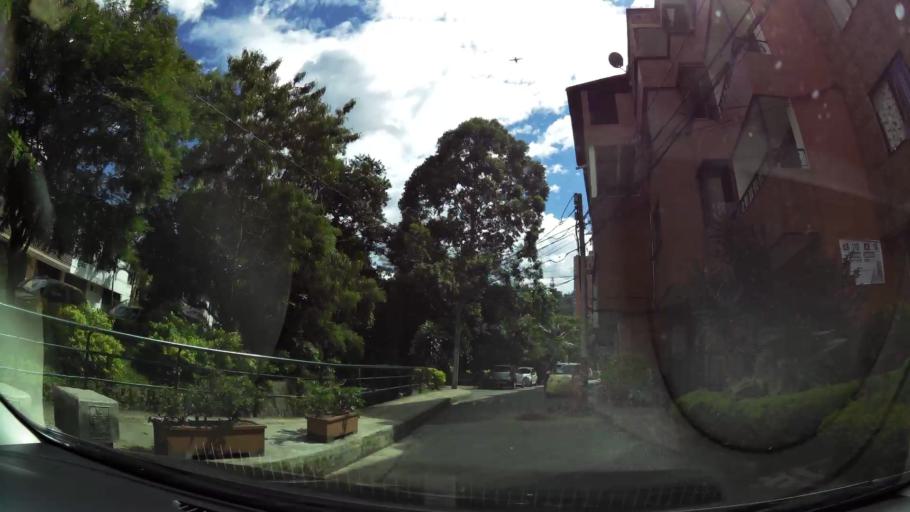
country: CO
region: Antioquia
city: Sabaneta
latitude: 6.1495
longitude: -75.6236
